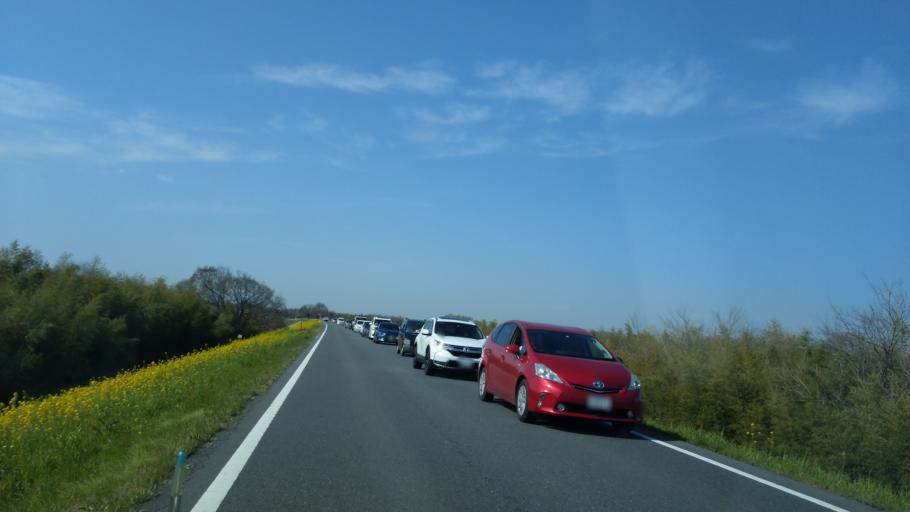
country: JP
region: Saitama
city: Okegawa
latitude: 35.9475
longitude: 139.5344
